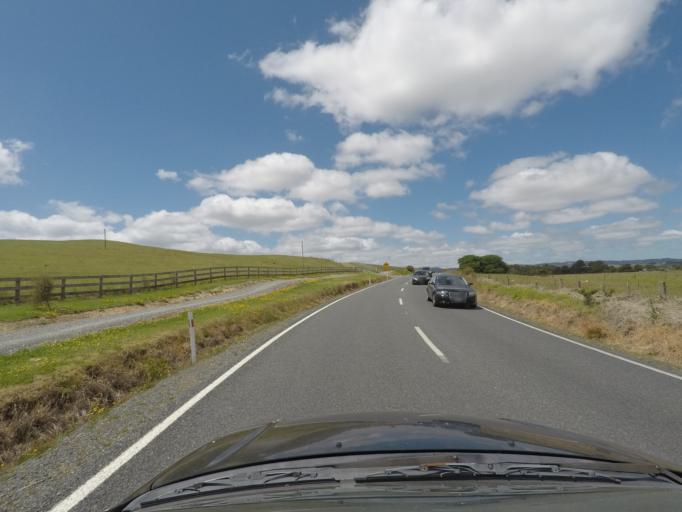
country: NZ
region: Northland
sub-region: Whangarei
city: Ruakaka
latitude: -35.9881
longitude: 174.4566
